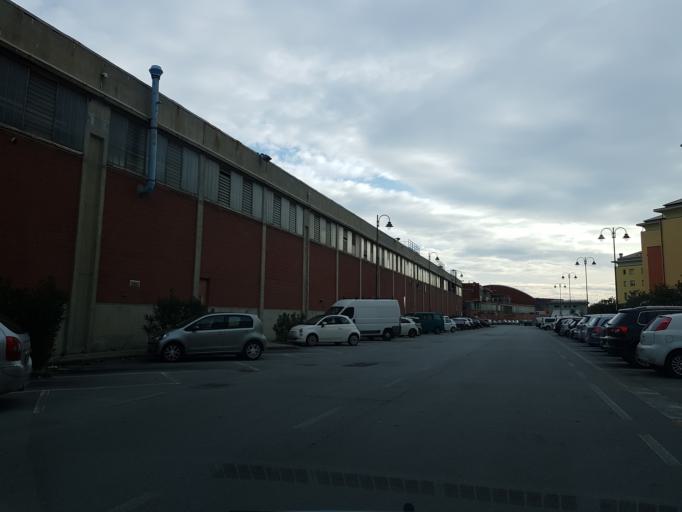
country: IT
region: Liguria
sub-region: Provincia di Genova
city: San Teodoro
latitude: 44.4200
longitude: 8.8494
